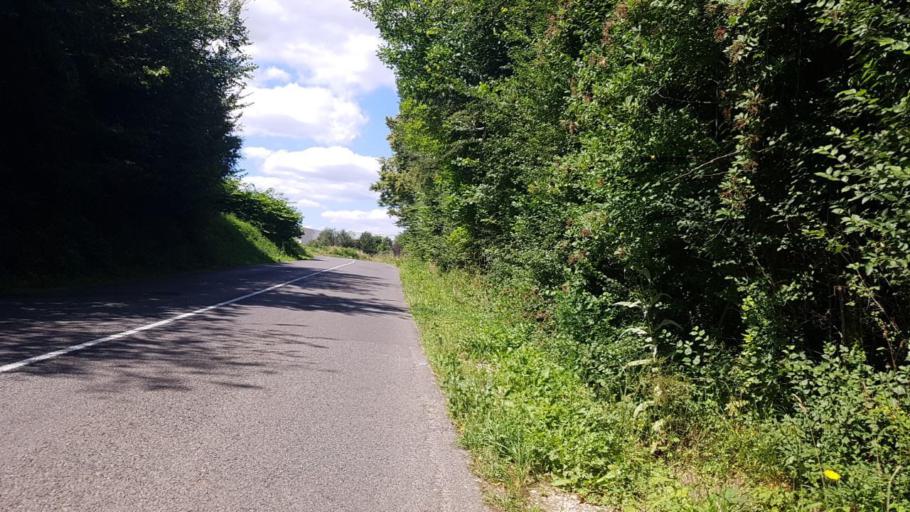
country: FR
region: Ile-de-France
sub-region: Departement de Seine-et-Marne
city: Moussy-le-Vieux
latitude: 49.0293
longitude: 2.6390
